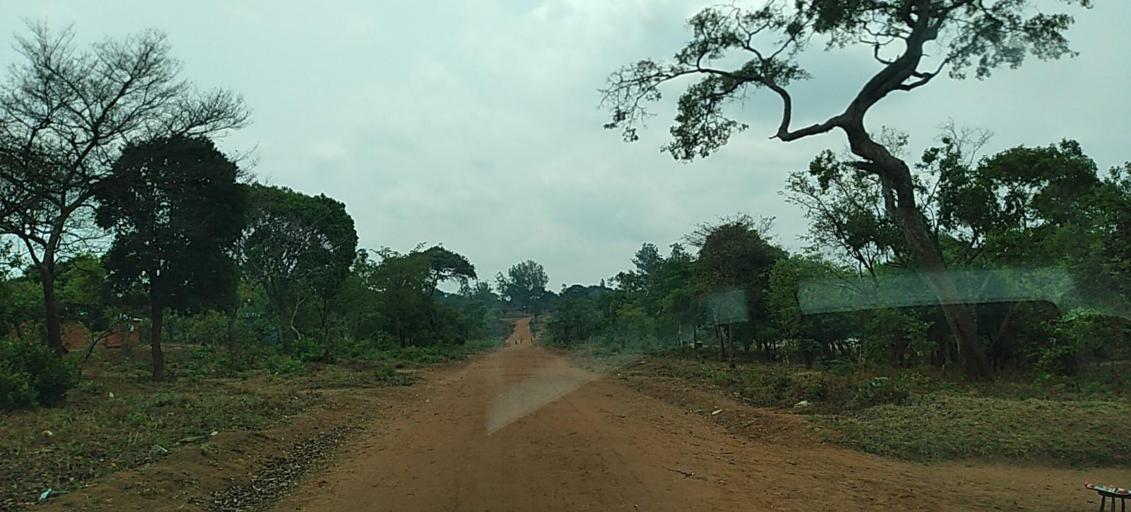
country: ZM
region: North-Western
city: Mwinilunga
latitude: -11.4454
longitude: 24.7484
